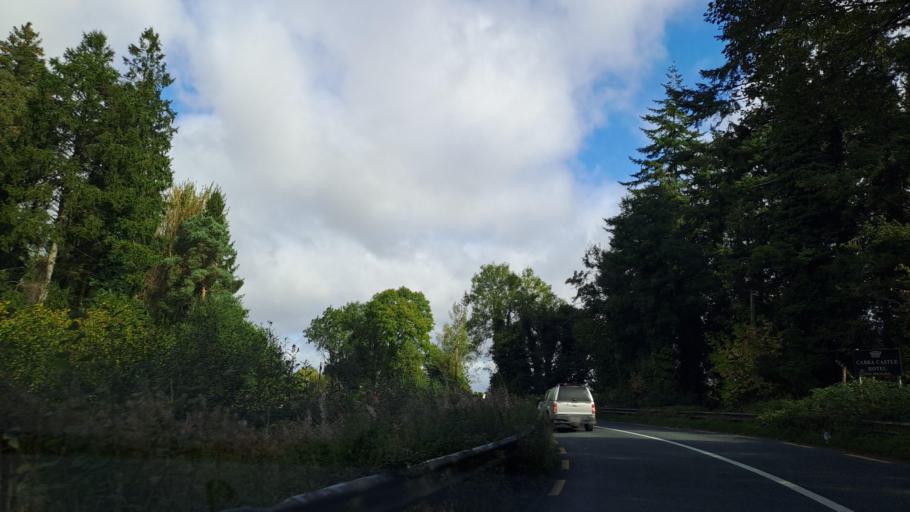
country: IE
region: Ulster
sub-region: An Cabhan
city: Kingscourt
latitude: 53.9142
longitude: -6.7853
